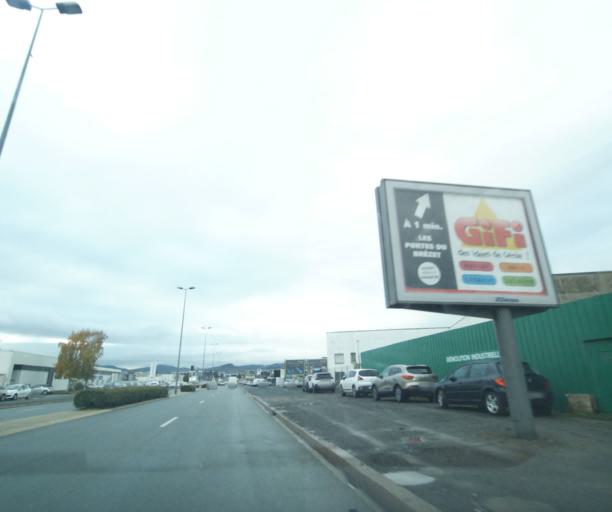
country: FR
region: Auvergne
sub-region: Departement du Puy-de-Dome
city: Aulnat
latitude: 45.7848
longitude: 3.1359
